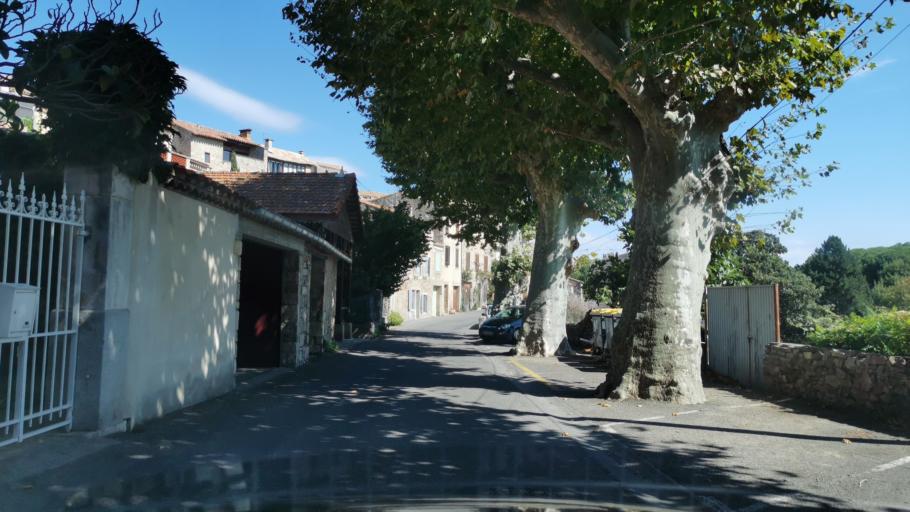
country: FR
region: Languedoc-Roussillon
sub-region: Departement de l'Aude
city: Caunes-Minervois
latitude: 43.3258
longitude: 2.5284
